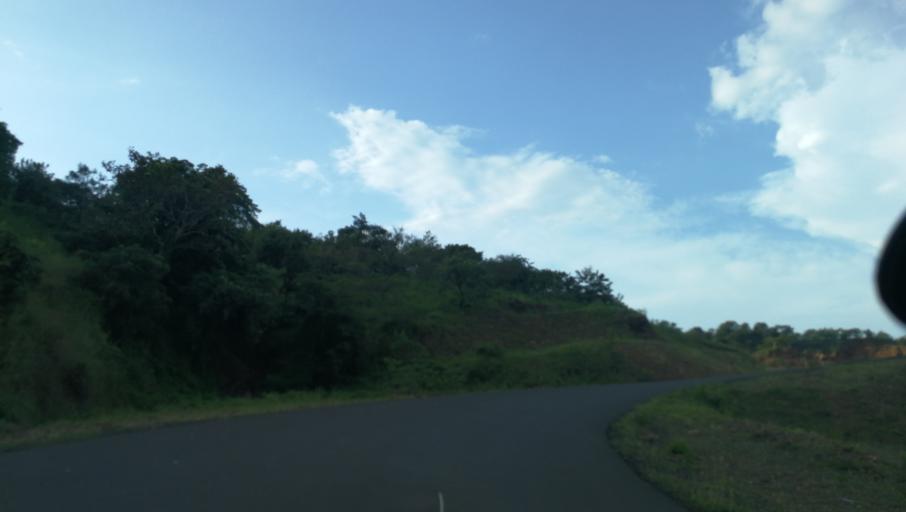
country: ET
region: Southern Nations, Nationalities, and People's Region
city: Areka
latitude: 6.8461
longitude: 37.2756
